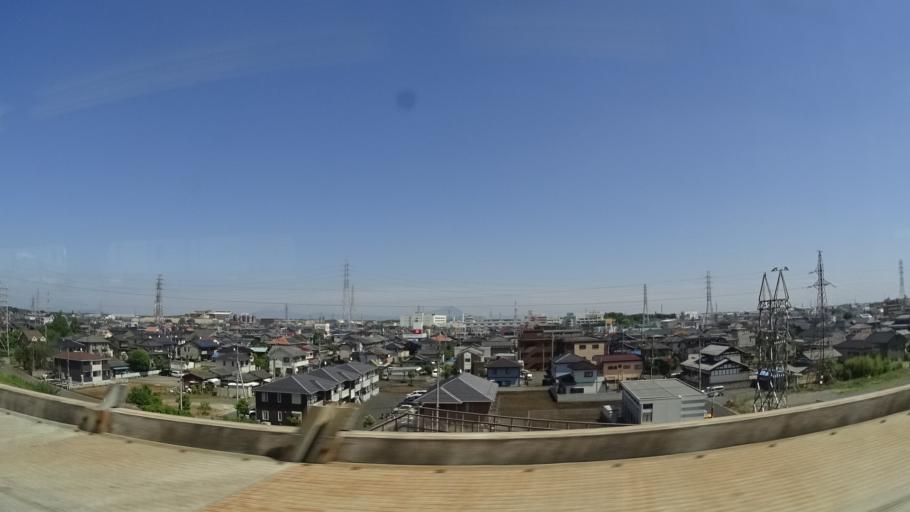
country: JP
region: Tochigi
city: Oyama
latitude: 36.3218
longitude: 139.8113
